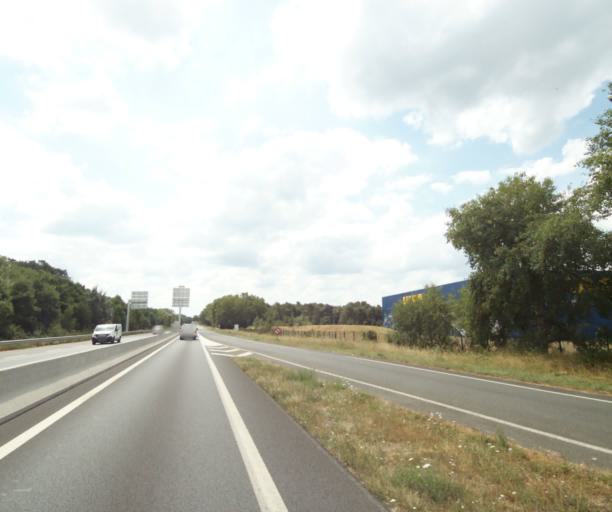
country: FR
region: Centre
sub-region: Departement du Loiret
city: Olivet
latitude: 47.8286
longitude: 1.9202
